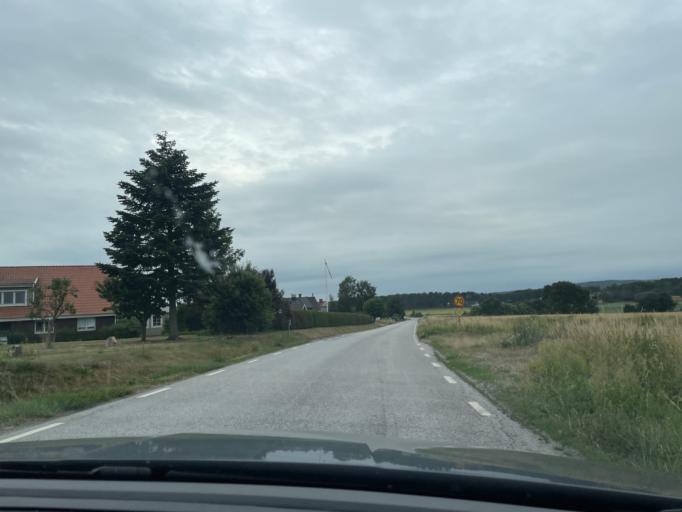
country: SE
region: Blekinge
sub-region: Solvesborgs Kommun
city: Soelvesborg
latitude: 56.0410
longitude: 14.6264
